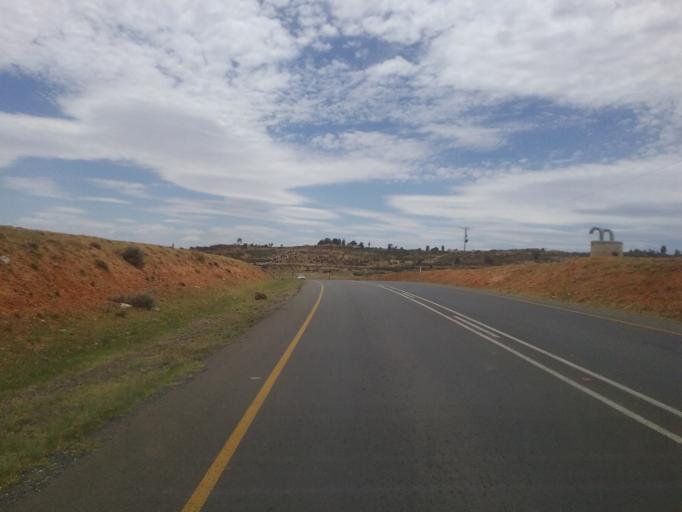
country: LS
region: Maseru
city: Maseru
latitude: -29.5058
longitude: 27.5274
